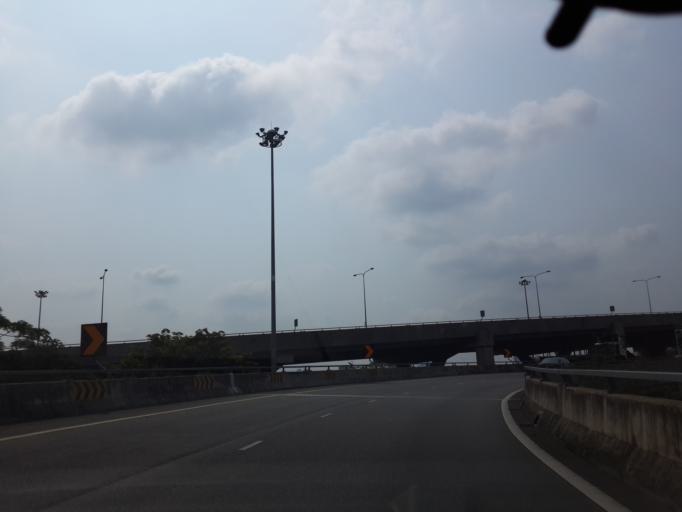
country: TH
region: Bangkok
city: Phra Khanong
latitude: 13.7025
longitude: 100.5912
